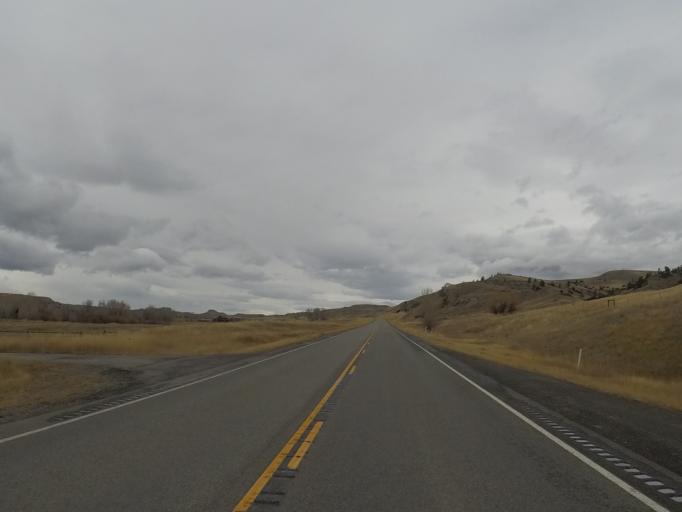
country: US
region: Montana
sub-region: Sweet Grass County
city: Big Timber
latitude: 45.9083
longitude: -109.9783
